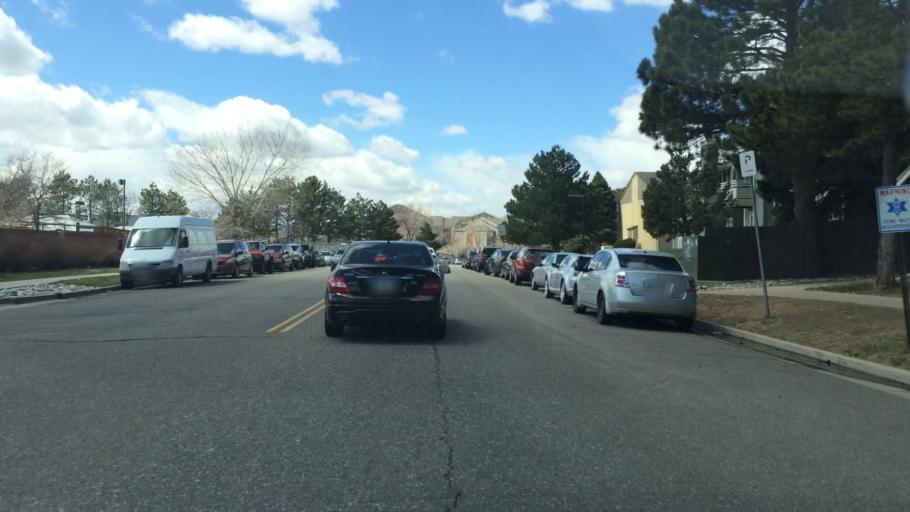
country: US
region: Colorado
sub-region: Arapahoe County
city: Centennial
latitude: 39.5972
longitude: -104.8716
